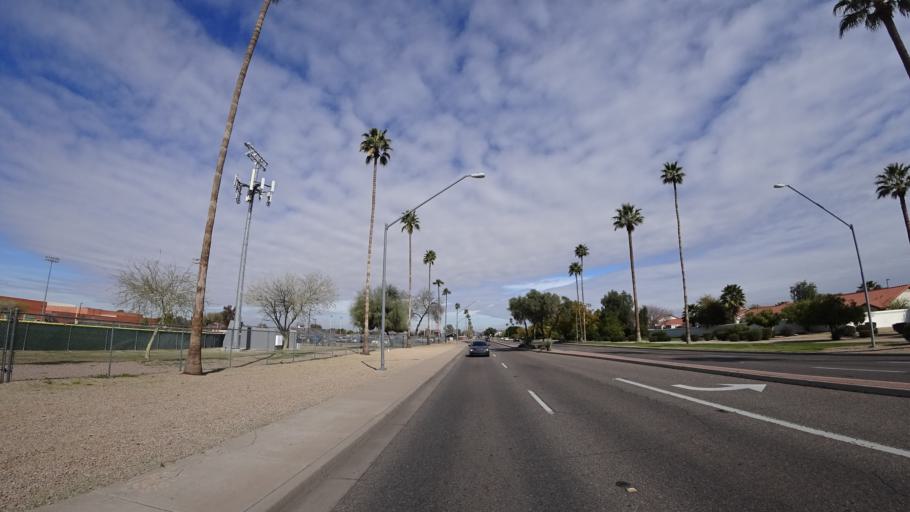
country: US
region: Arizona
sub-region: Maricopa County
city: Peoria
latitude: 33.6004
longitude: -112.1861
